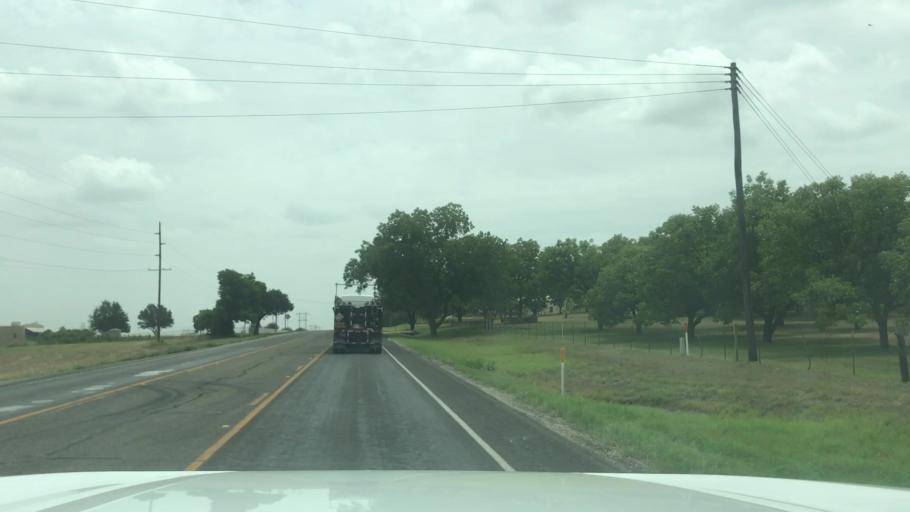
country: US
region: Texas
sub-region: Bosque County
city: Clifton
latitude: 31.7704
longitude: -97.5699
